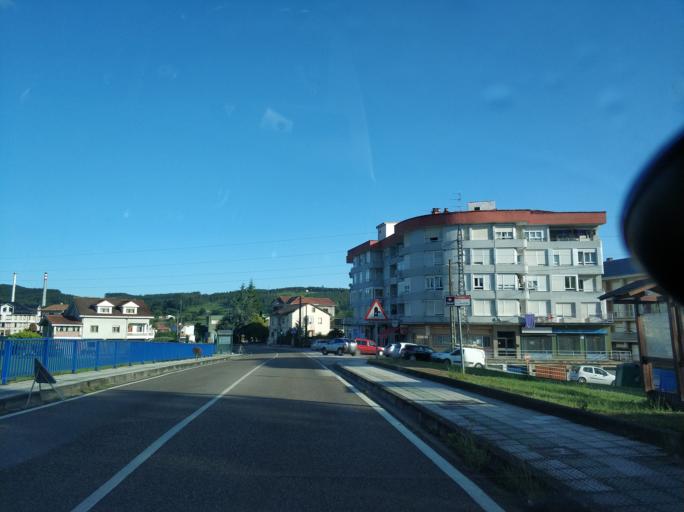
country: ES
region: Cantabria
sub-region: Provincia de Cantabria
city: Puente Viesgo
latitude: 43.3566
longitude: -3.9628
